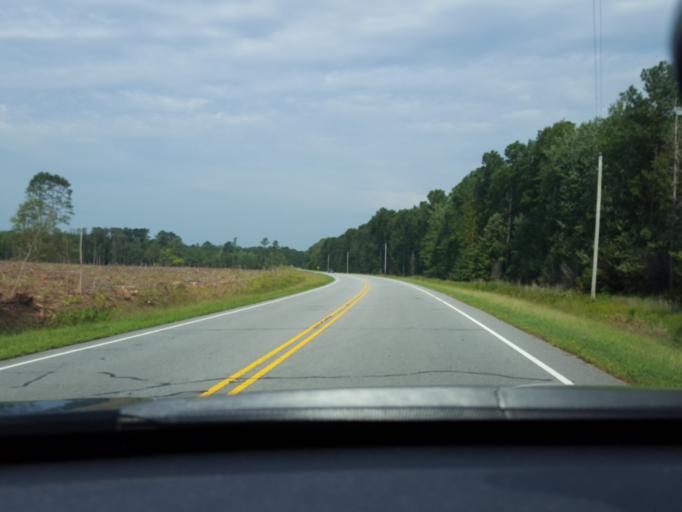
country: US
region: North Carolina
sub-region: Washington County
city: Plymouth
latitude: 35.9673
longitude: -76.7513
